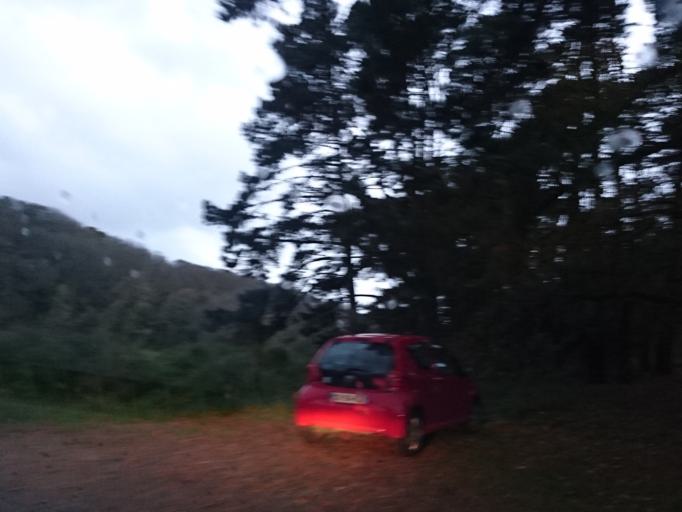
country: FR
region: Brittany
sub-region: Departement du Finistere
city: Le Conquet
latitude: 48.3667
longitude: -4.7469
